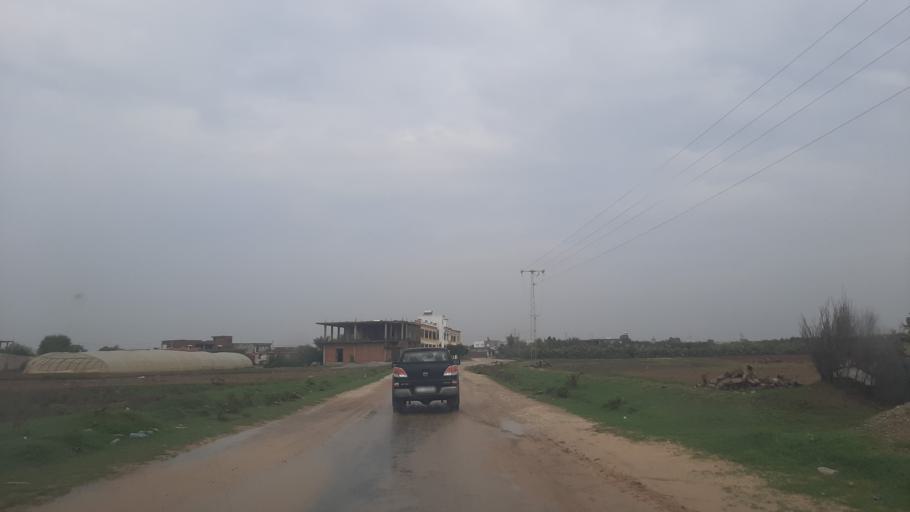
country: TN
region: Al Munastir
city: Sidi Bin Nur
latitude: 35.4747
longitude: 10.8772
